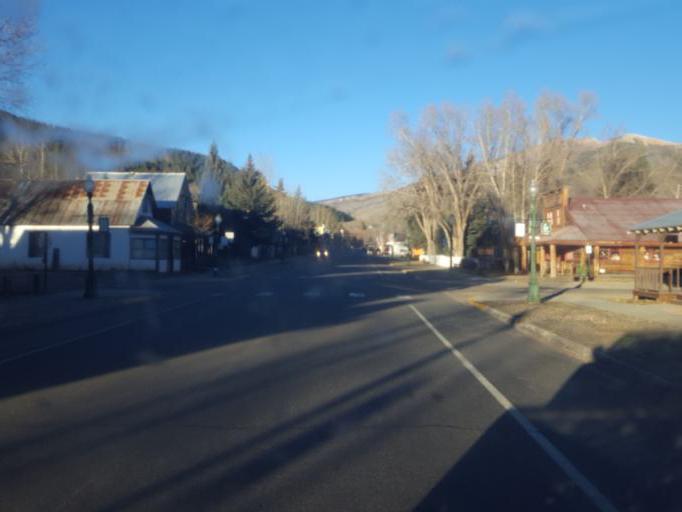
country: US
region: Colorado
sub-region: Gunnison County
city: Crested Butte
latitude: 38.8698
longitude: -106.9819
